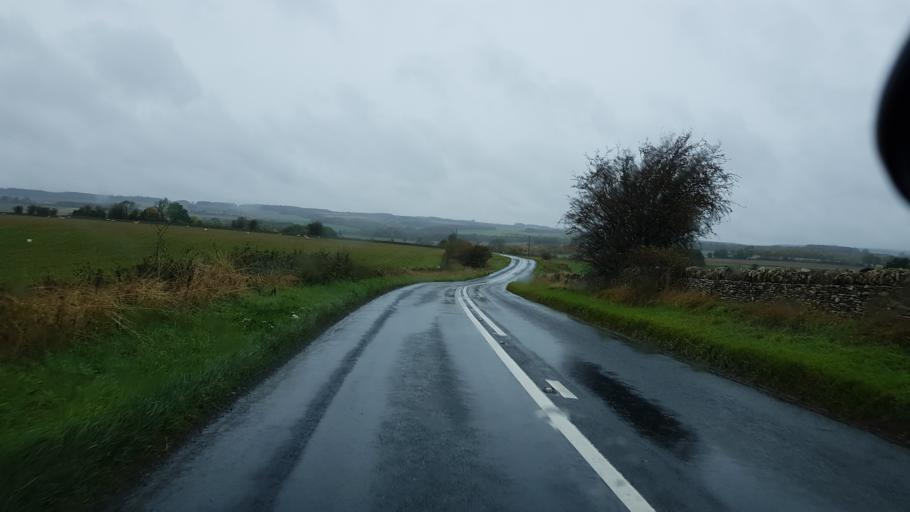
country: GB
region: England
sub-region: Gloucestershire
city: Stow on the Wold
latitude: 51.9454
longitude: -1.7819
